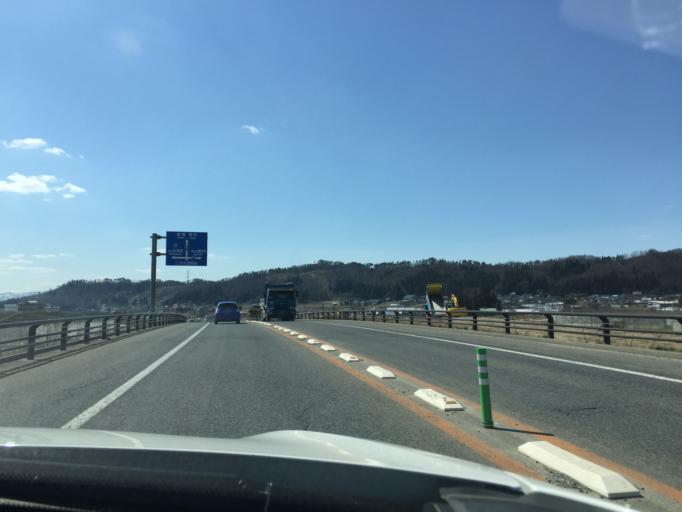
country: JP
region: Yamagata
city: Nagai
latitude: 38.0584
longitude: 140.1132
